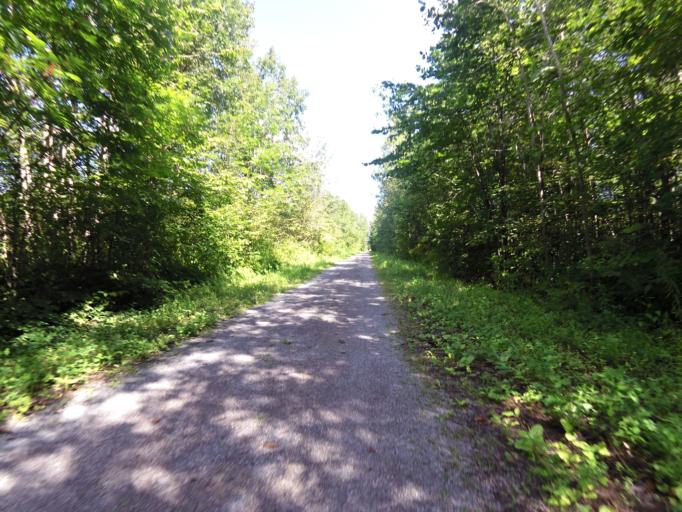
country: CA
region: Ontario
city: Ottawa
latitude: 45.1991
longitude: -75.6232
